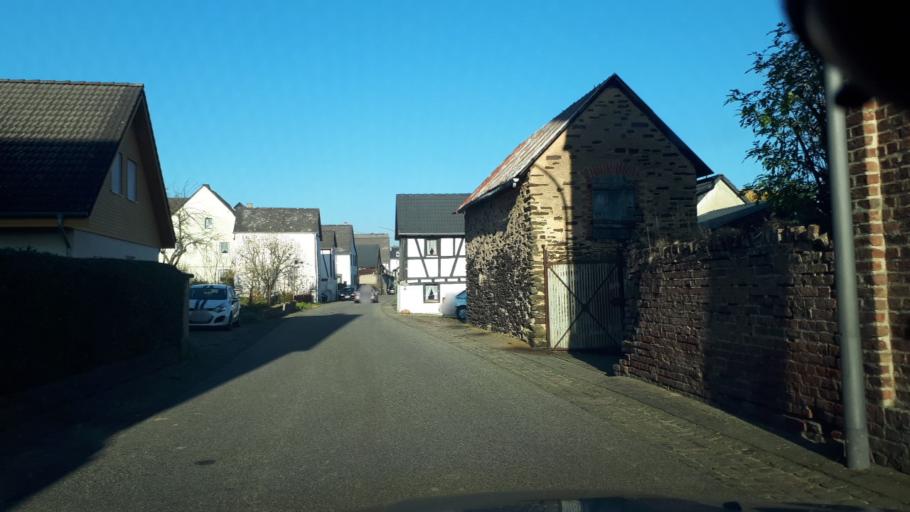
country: DE
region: Rheinland-Pfalz
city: Brieden
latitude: 50.1867
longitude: 7.2638
